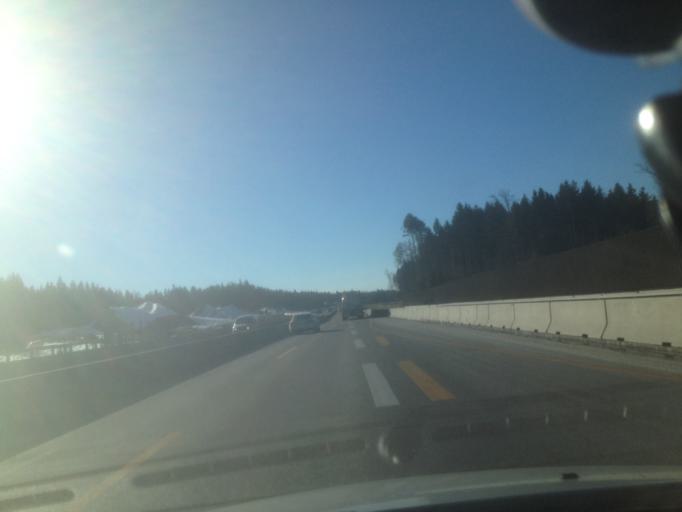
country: DE
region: Bavaria
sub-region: Swabia
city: Horgau
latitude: 48.4110
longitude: 10.6443
